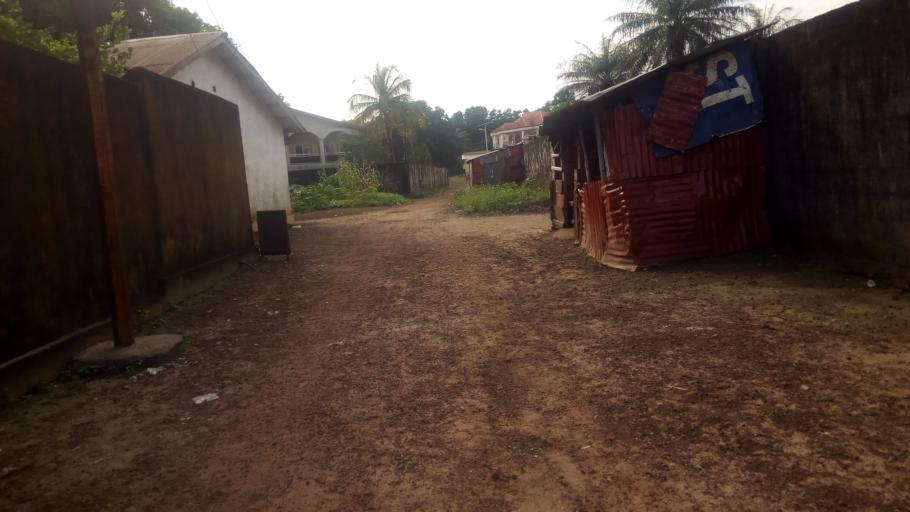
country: GN
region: Kindia
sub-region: Prefecture de Dubreka
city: Dubreka
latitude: 9.6482
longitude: -13.5327
